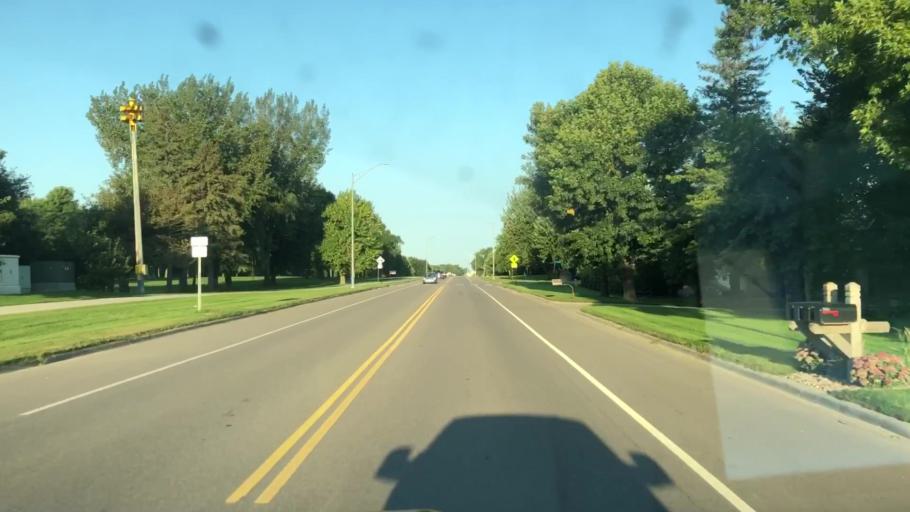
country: US
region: Minnesota
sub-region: Nobles County
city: Worthington
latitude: 43.6310
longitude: -95.6189
